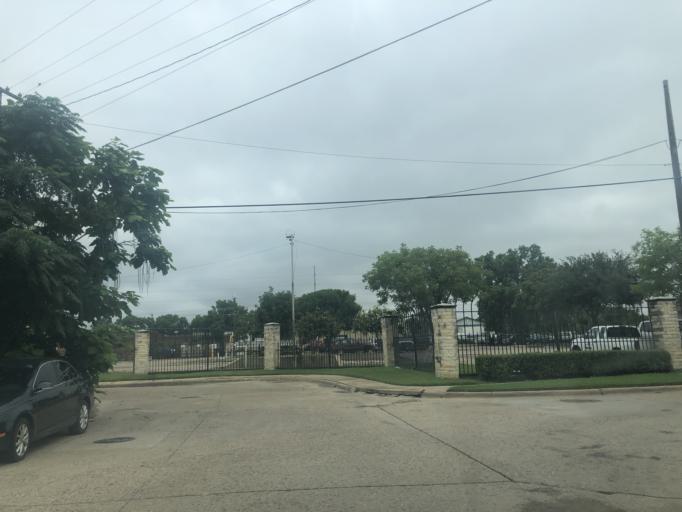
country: US
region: Texas
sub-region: Dallas County
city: Dallas
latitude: 32.7771
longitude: -96.8508
